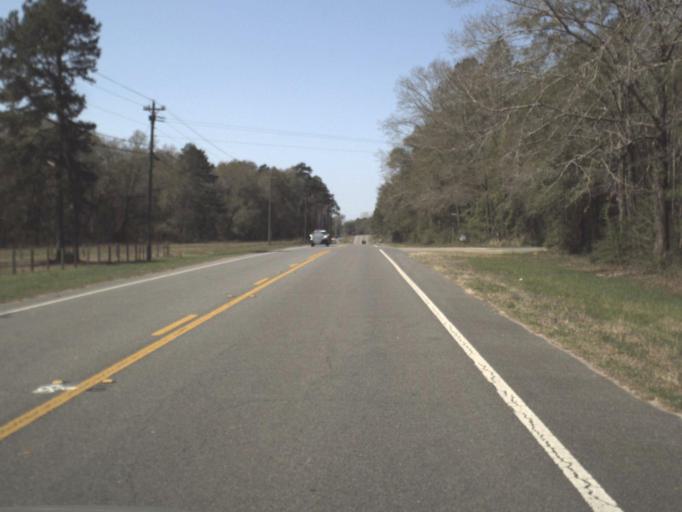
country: US
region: Florida
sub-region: Gadsden County
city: Havana
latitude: 30.6098
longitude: -84.4641
